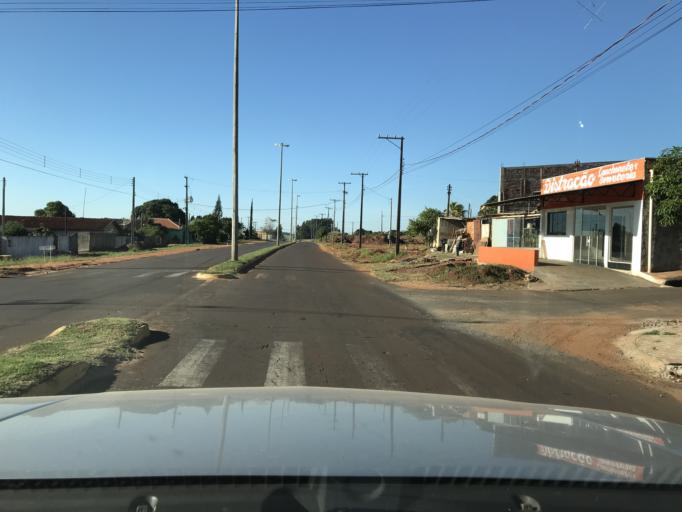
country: BR
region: Parana
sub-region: Ipora
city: Ipora
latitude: -24.0033
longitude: -53.7001
